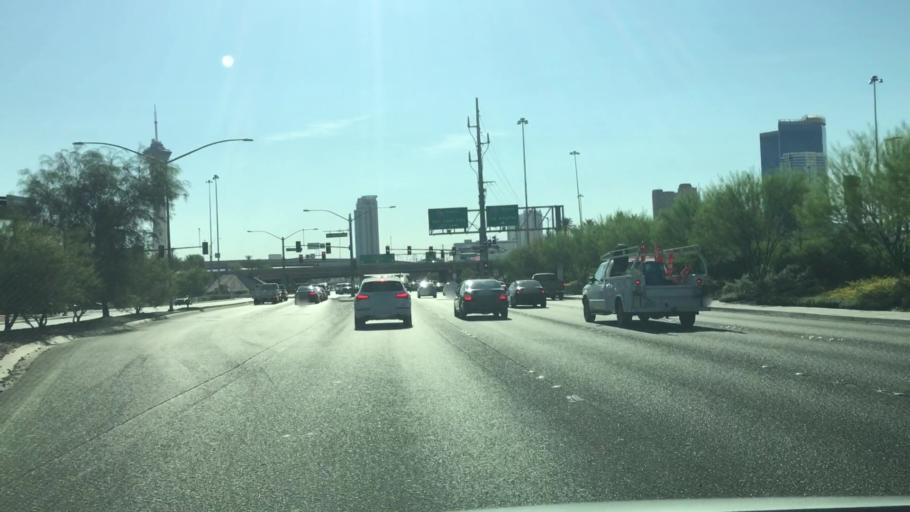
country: US
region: Nevada
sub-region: Clark County
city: Las Vegas
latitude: 36.1442
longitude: -115.1745
